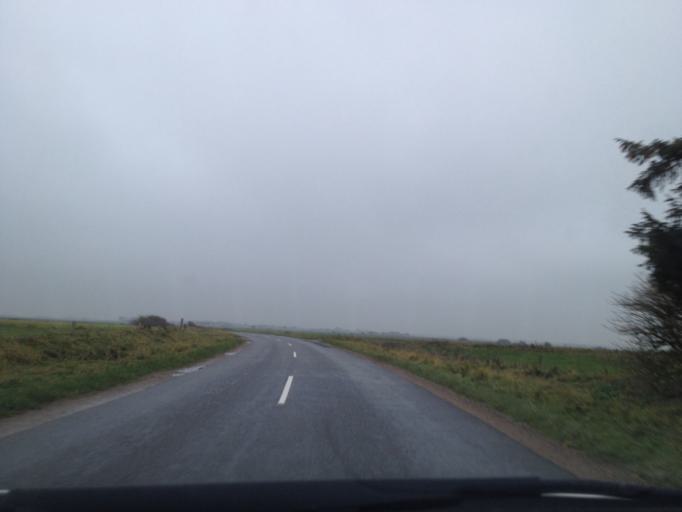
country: DK
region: South Denmark
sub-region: Tonder Kommune
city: Sherrebek
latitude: 55.1080
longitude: 8.7274
